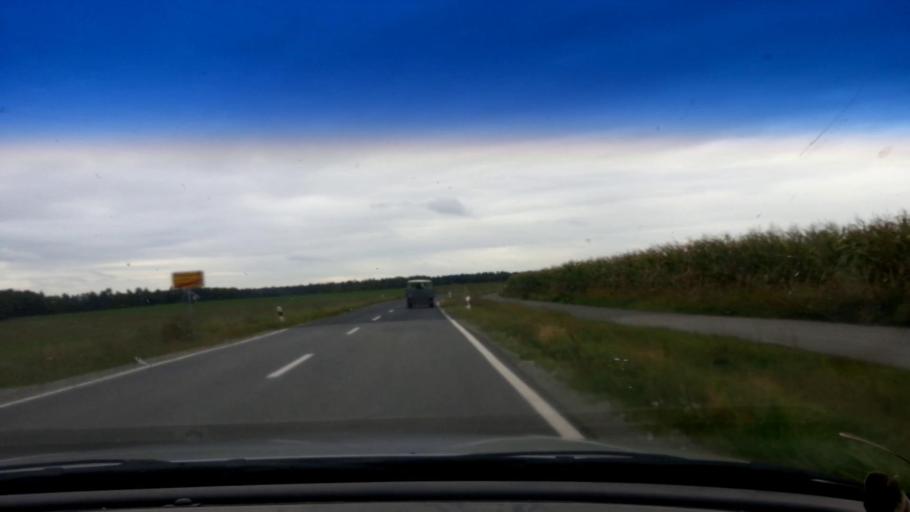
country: DE
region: Bavaria
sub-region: Upper Franconia
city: Priesendorf
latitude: 49.8894
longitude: 10.6525
